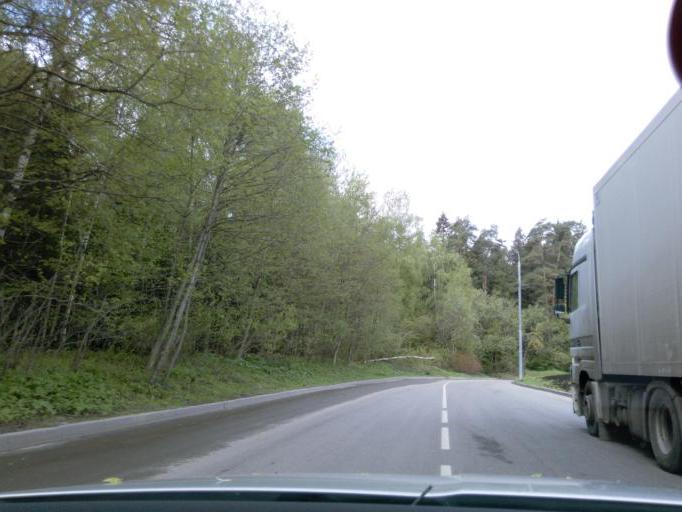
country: RU
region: Moscow
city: Zelenograd
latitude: 56.0053
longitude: 37.1805
